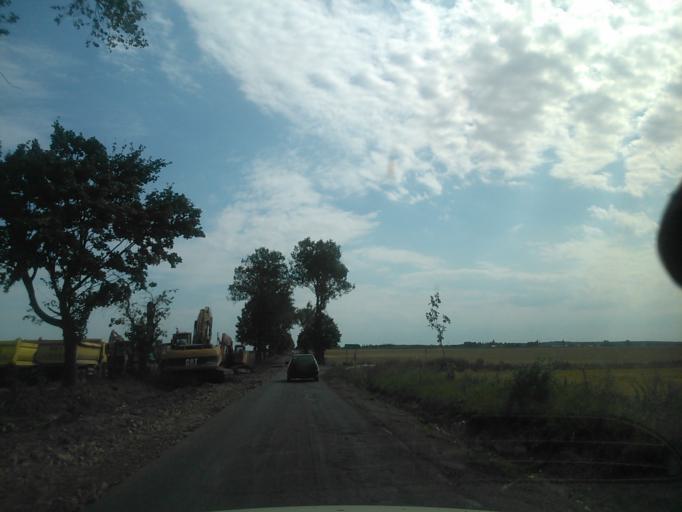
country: PL
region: Warmian-Masurian Voivodeship
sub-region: Powiat dzialdowski
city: Ilowo -Osada
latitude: 53.1878
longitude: 20.2813
